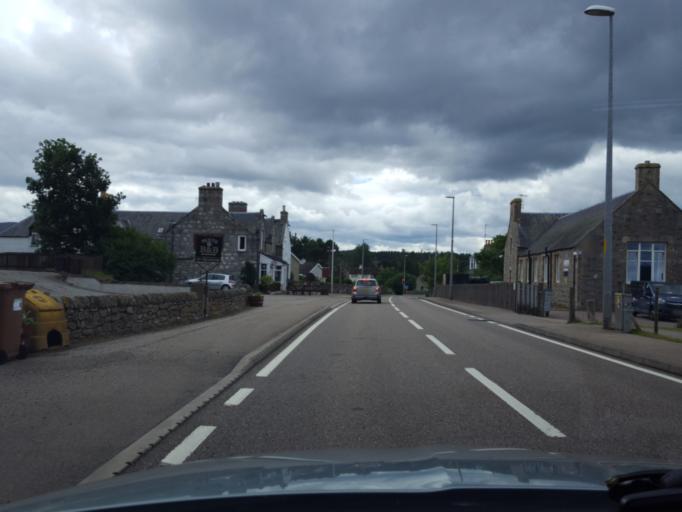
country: GB
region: Scotland
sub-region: Highland
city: Grantown on Spey
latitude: 57.3388
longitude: -3.5375
